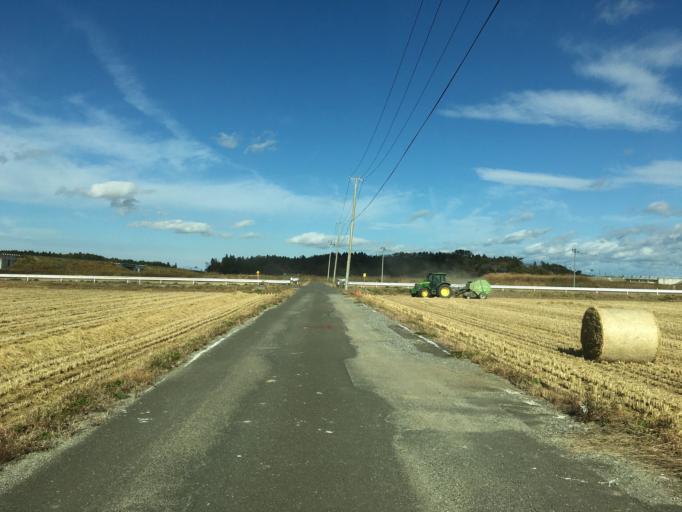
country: JP
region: Miyagi
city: Marumori
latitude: 37.8881
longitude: 140.9276
